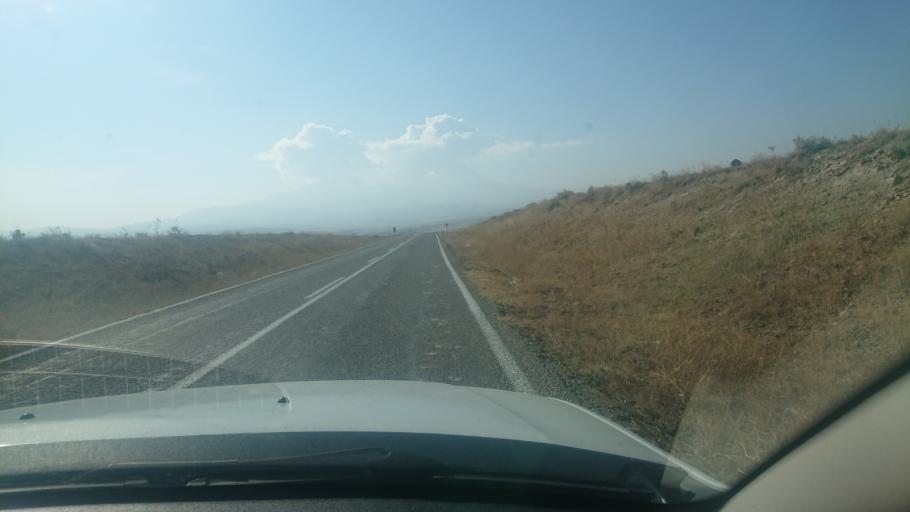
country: TR
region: Aksaray
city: Guzelyurt
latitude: 38.2492
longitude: 34.3276
